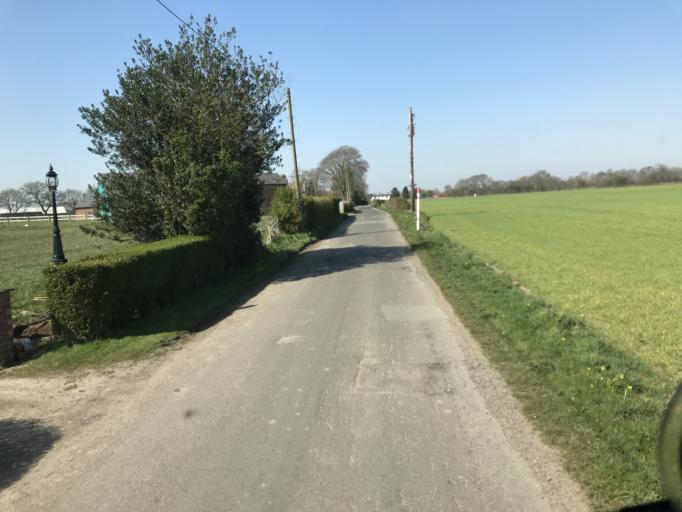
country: GB
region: England
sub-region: Trafford
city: Partington
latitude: 53.4227
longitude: -2.4701
